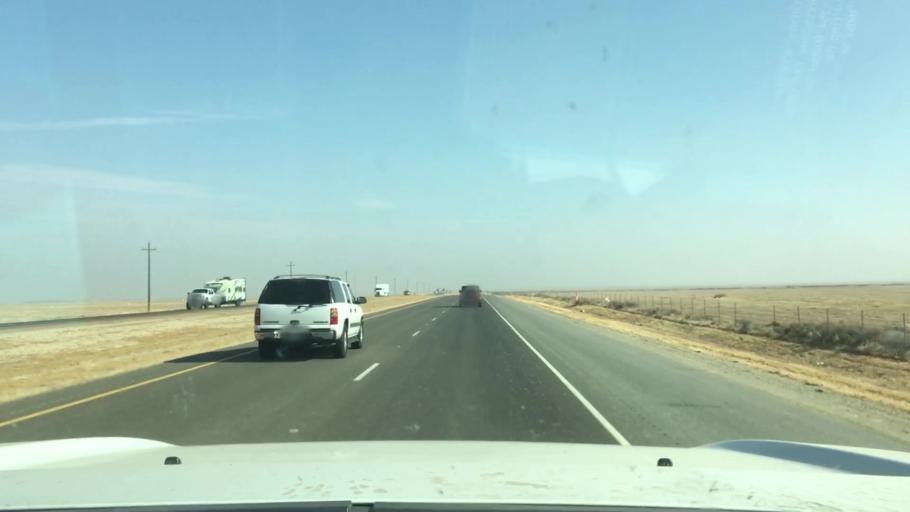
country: US
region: California
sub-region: Kern County
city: Lost Hills
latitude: 35.6152
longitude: -119.8398
